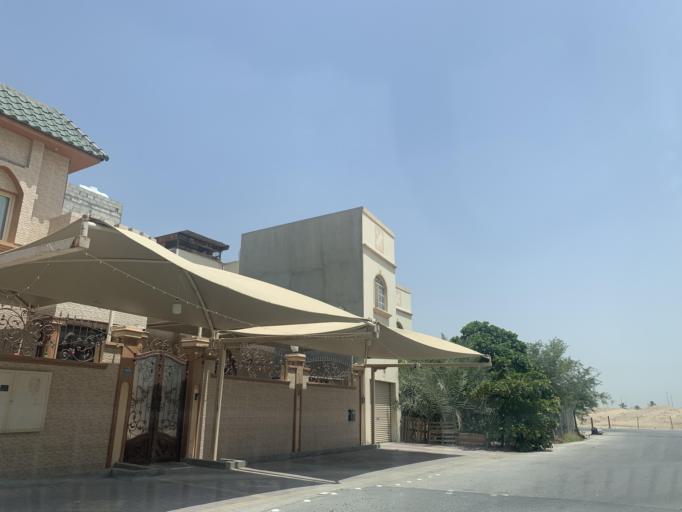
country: BH
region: Central Governorate
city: Madinat Hamad
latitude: 26.1447
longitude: 50.5059
